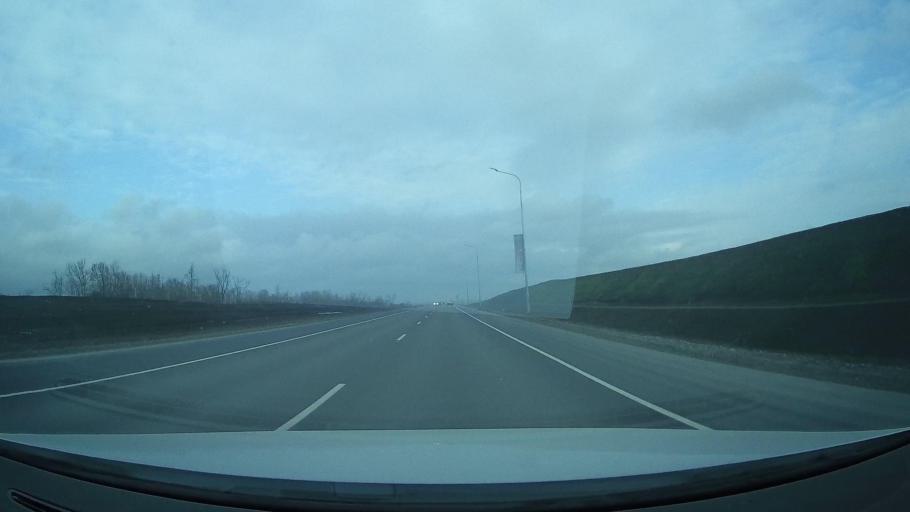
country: RU
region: Rostov
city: Grushevskaya
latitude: 47.4215
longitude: 39.8632
